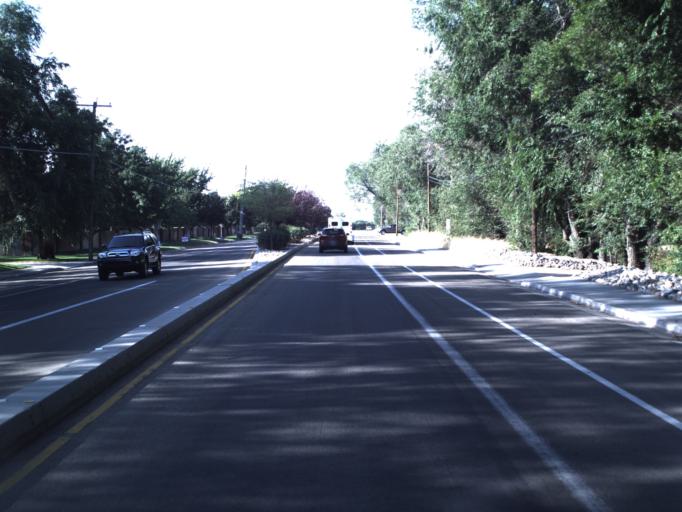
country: US
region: Utah
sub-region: Utah County
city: Alpine
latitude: 40.4264
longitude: -111.7858
